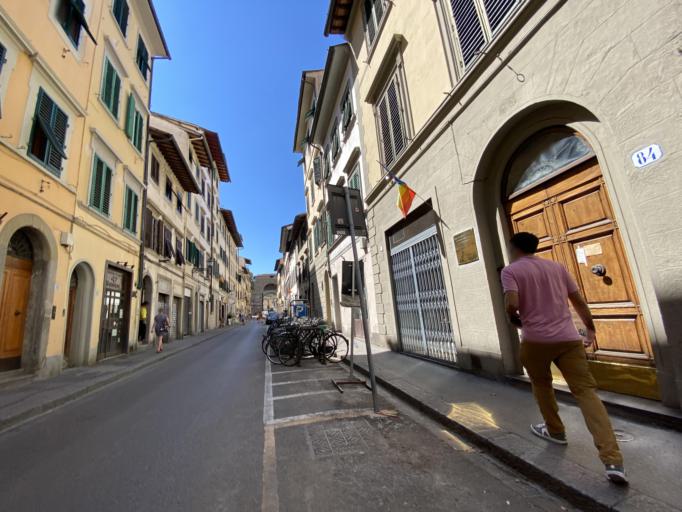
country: IT
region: Tuscany
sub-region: Province of Florence
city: Florence
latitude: 43.7620
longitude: 11.2430
